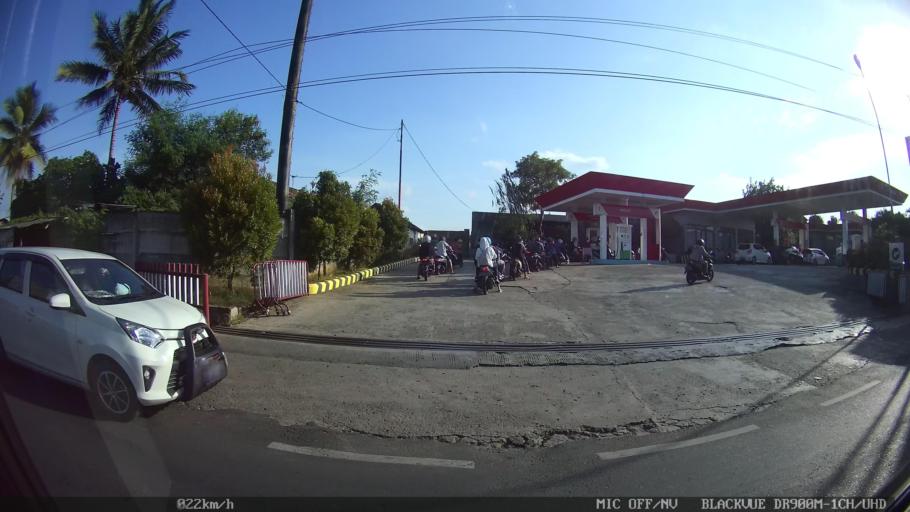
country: ID
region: Lampung
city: Kedaton
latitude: -5.3940
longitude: 105.2324
